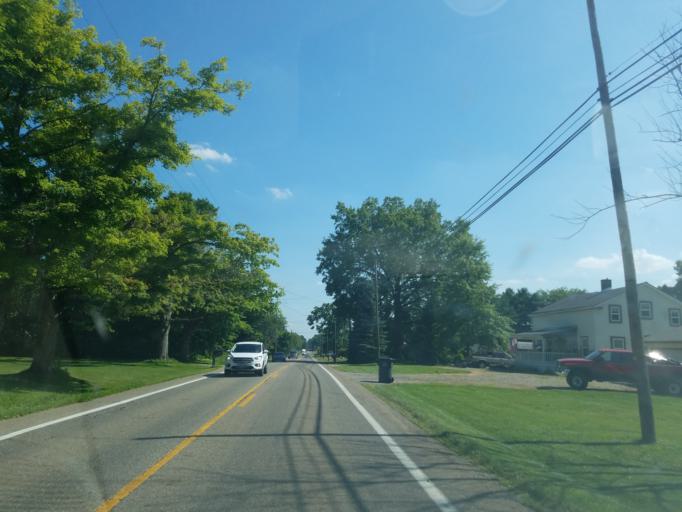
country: US
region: Ohio
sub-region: Portage County
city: Ravenna
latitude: 41.2000
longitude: -81.2461
